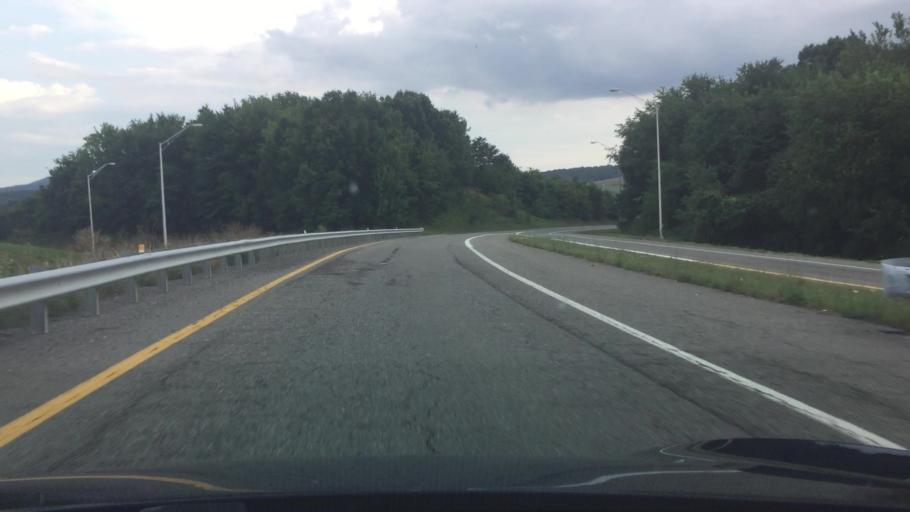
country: US
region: Virginia
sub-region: Montgomery County
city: Christiansburg
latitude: 37.1304
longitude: -80.3725
